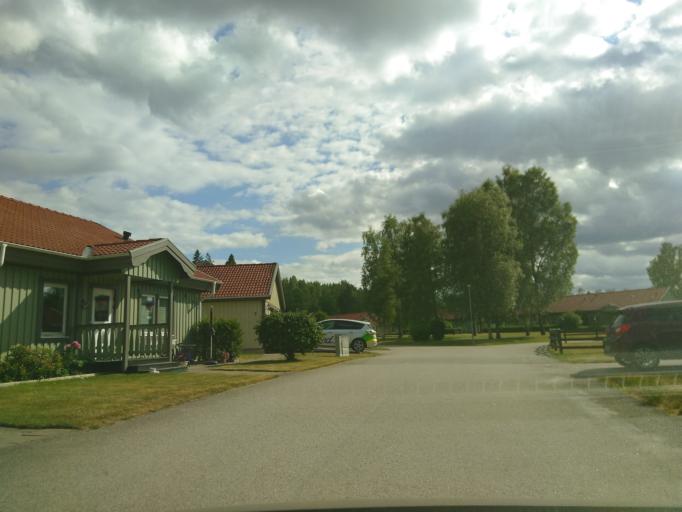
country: SE
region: Vaestra Goetaland
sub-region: Herrljunga Kommun
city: Herrljunga
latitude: 58.0584
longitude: 13.0948
